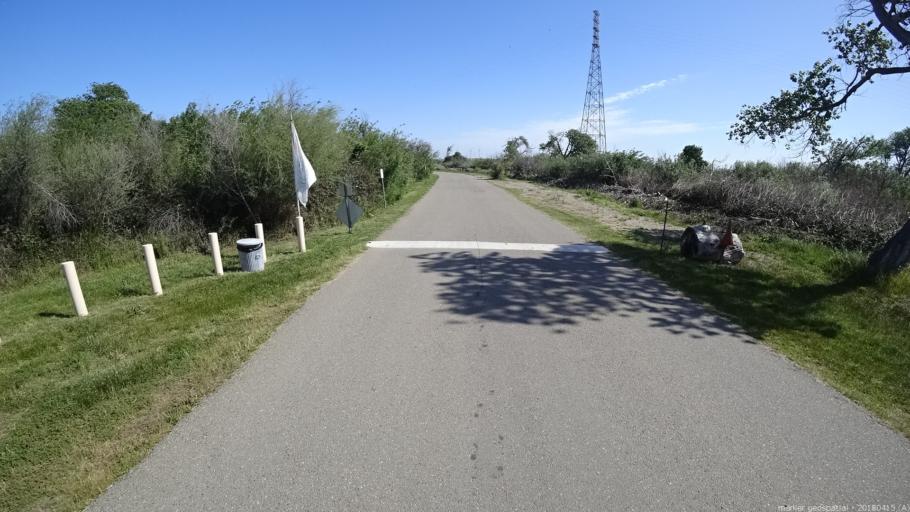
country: US
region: California
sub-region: Contra Costa County
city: Antioch
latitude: 38.0584
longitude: -121.7863
